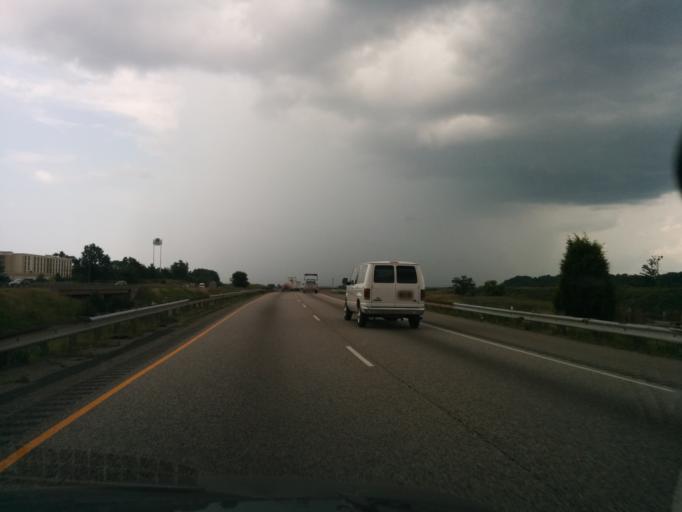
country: US
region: Virginia
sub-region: Augusta County
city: Verona
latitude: 38.1655
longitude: -79.0112
